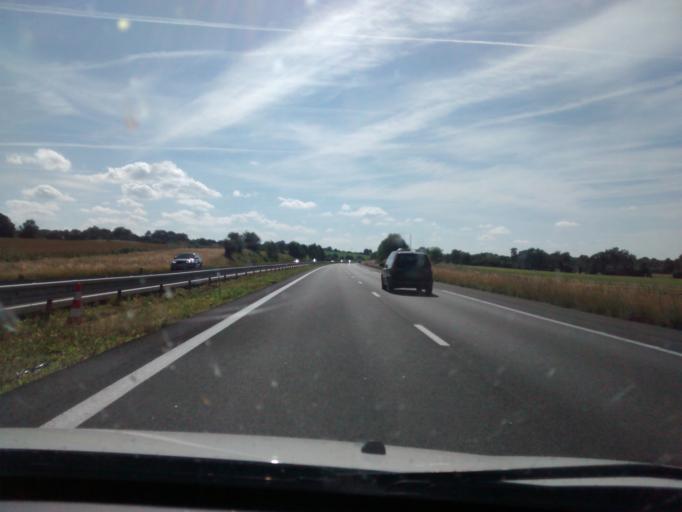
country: FR
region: Pays de la Loire
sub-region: Departement de la Mayenne
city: Vaiges
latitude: 48.0509
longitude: -0.4404
